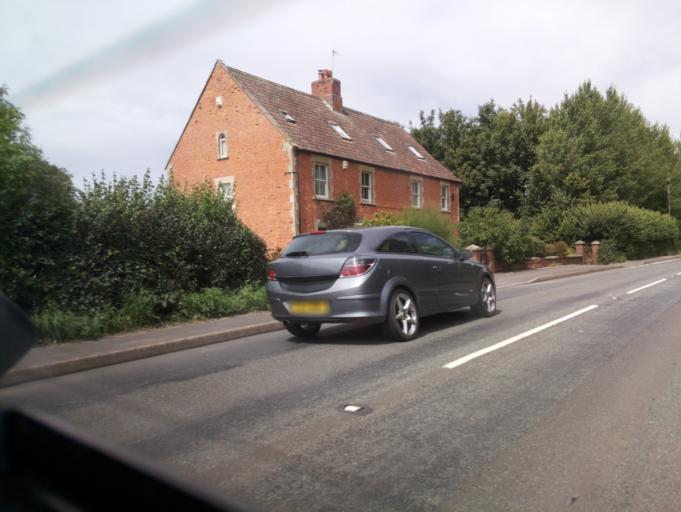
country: GB
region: England
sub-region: Somerset
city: Wells
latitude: 51.1964
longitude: -2.6665
